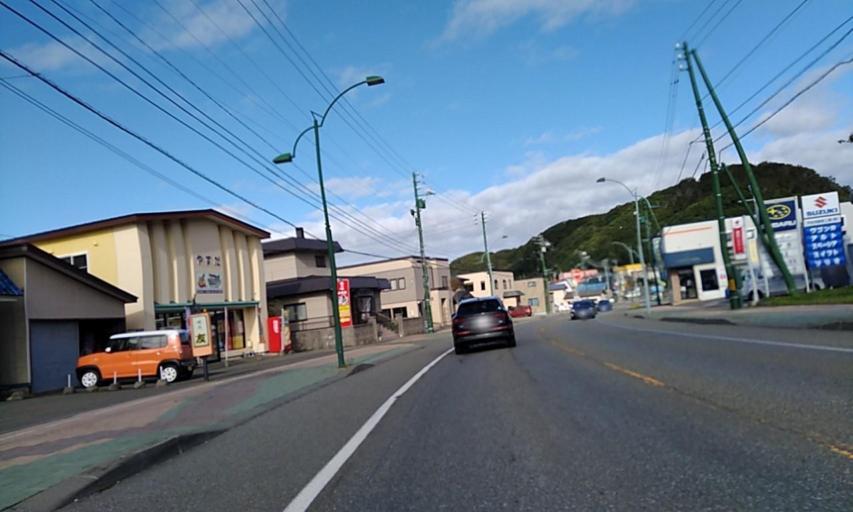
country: JP
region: Hokkaido
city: Shizunai-furukawacho
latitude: 42.2489
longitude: 142.5547
